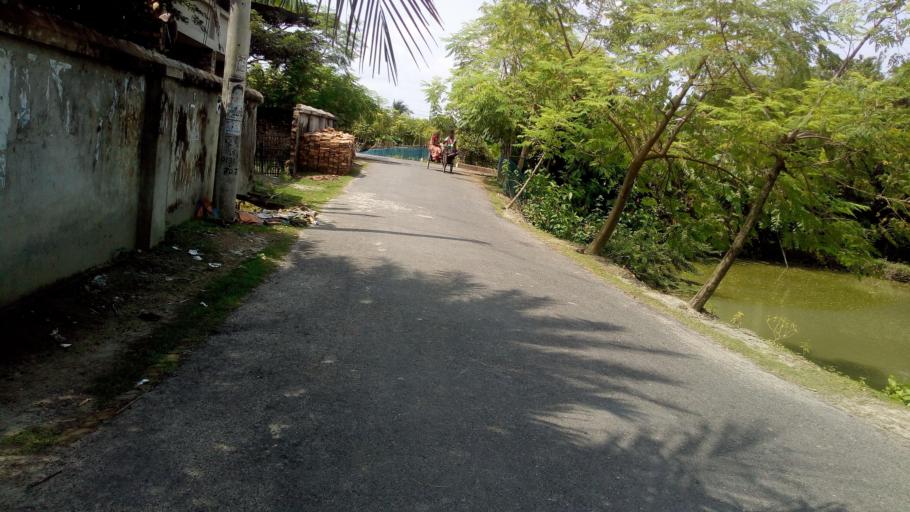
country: BD
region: Khulna
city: Phultala
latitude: 22.5728
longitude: 89.4570
